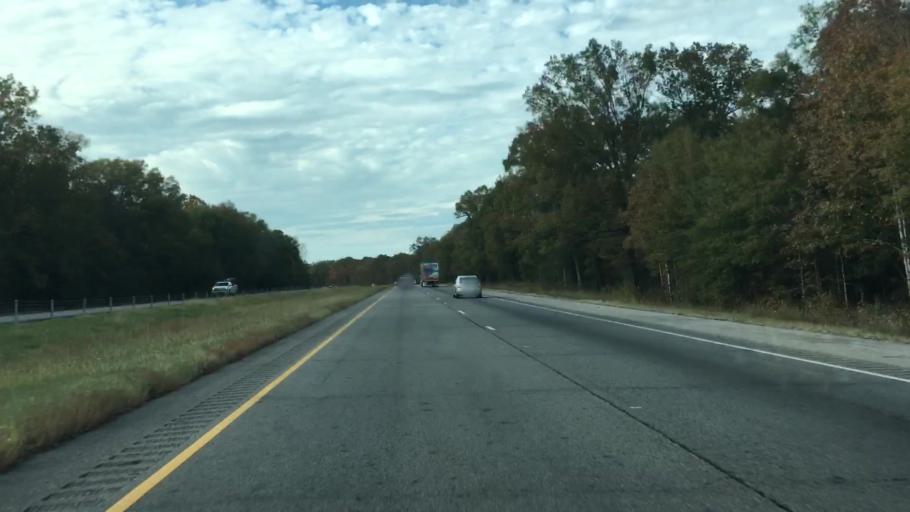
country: US
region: Arkansas
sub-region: Pope County
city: Atkins
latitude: 35.2423
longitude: -92.8607
